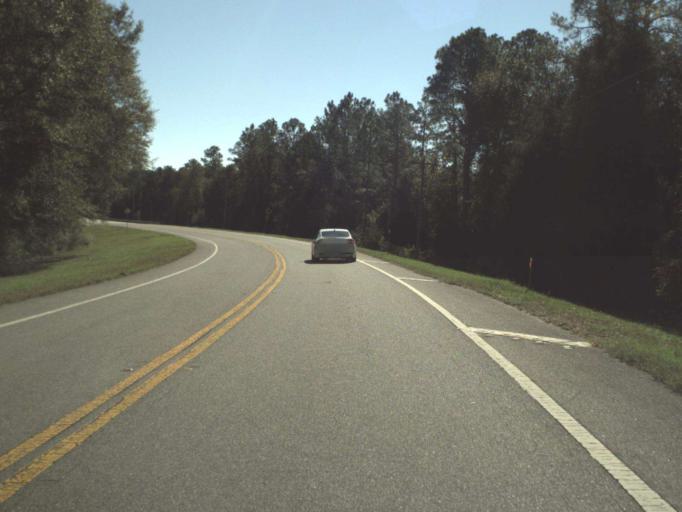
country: US
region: Florida
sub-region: Okaloosa County
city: Crestview
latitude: 30.8359
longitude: -86.7358
